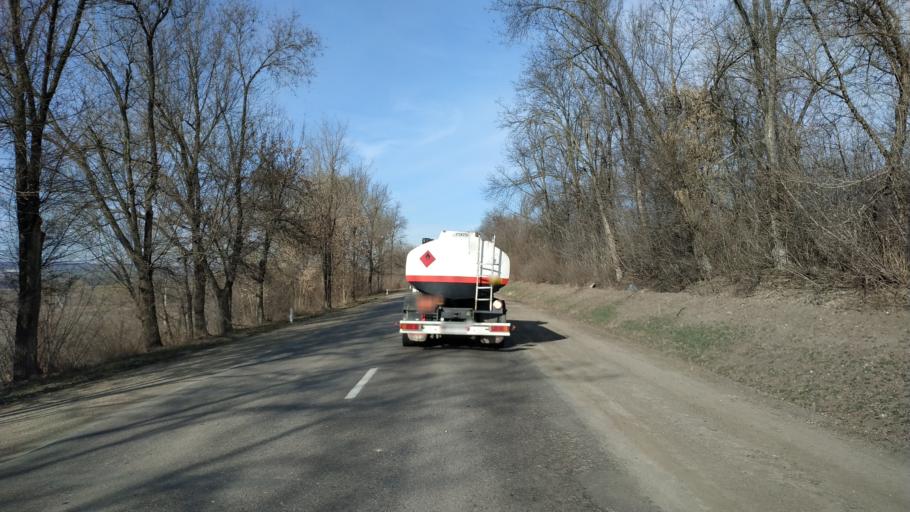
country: MD
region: Laloveni
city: Ialoveni
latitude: 46.9552
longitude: 28.7534
